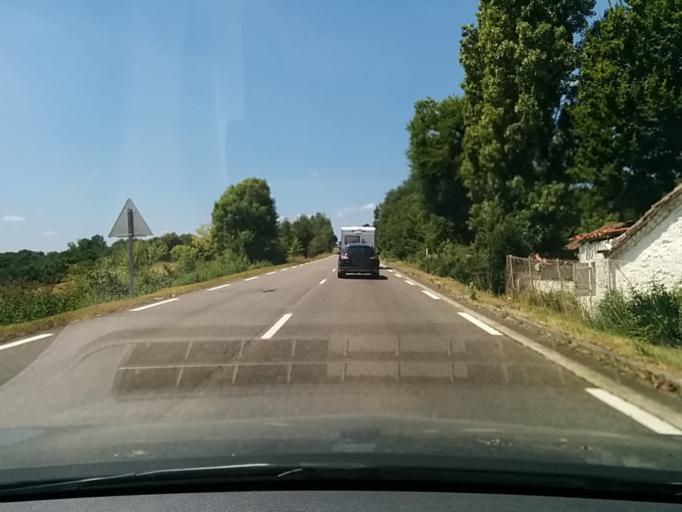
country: FR
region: Midi-Pyrenees
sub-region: Departement du Gers
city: Vic-Fezensac
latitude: 43.7593
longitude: 0.2092
